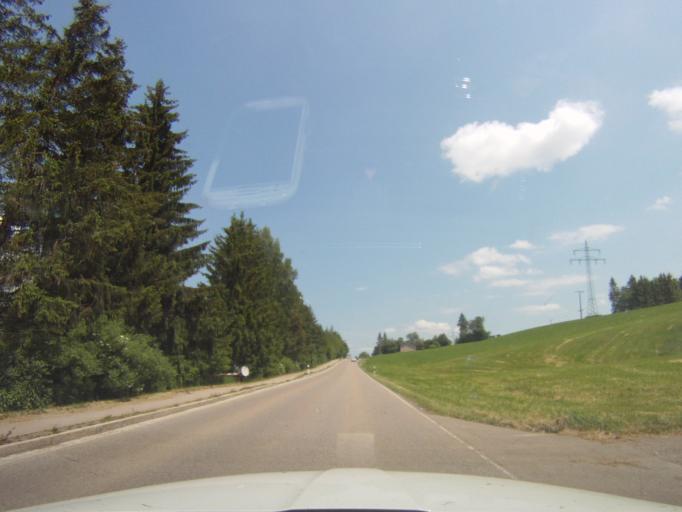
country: DE
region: Bavaria
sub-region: Swabia
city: Oy-Mittelberg
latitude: 47.6086
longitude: 10.4458
